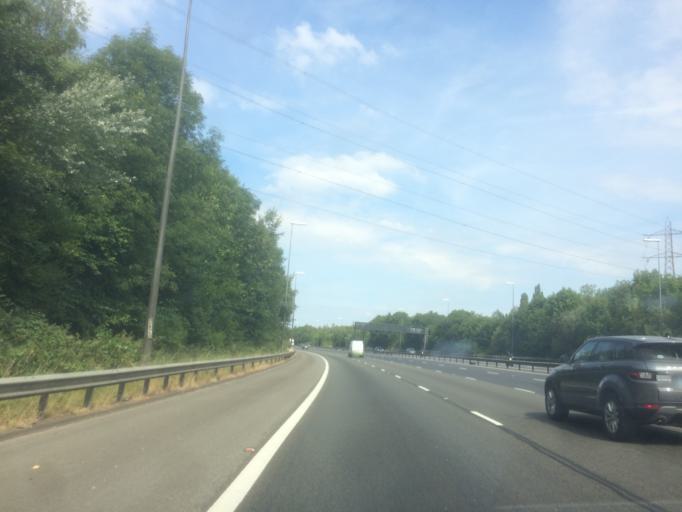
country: GB
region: England
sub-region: Buckinghamshire
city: Gerrards Cross
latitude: 51.5807
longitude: -0.5844
